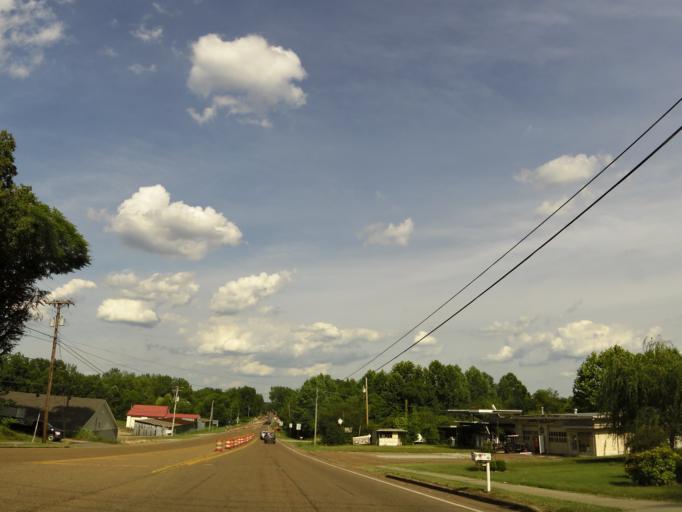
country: US
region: Tennessee
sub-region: Carroll County
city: Bruceton
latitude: 36.0379
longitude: -88.2375
